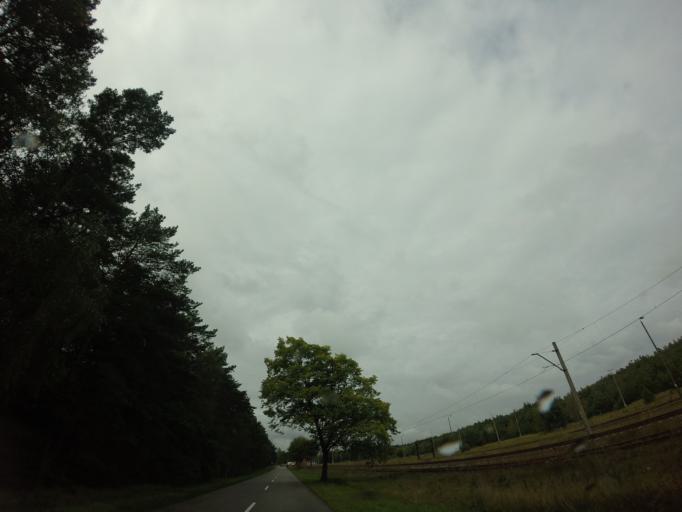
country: PL
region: West Pomeranian Voivodeship
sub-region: Swinoujscie
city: Swinoujscie
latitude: 53.8989
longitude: 14.3068
